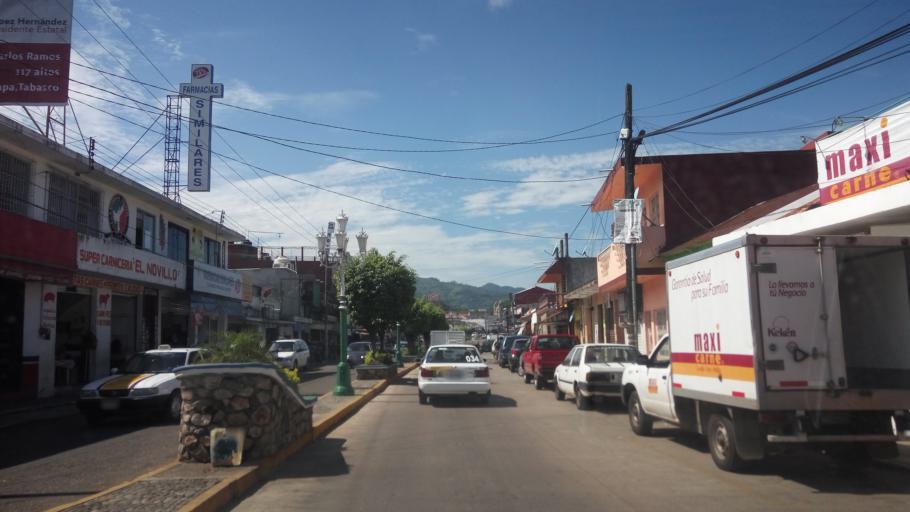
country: MX
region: Tabasco
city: Teapa
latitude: 17.5534
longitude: -92.9510
